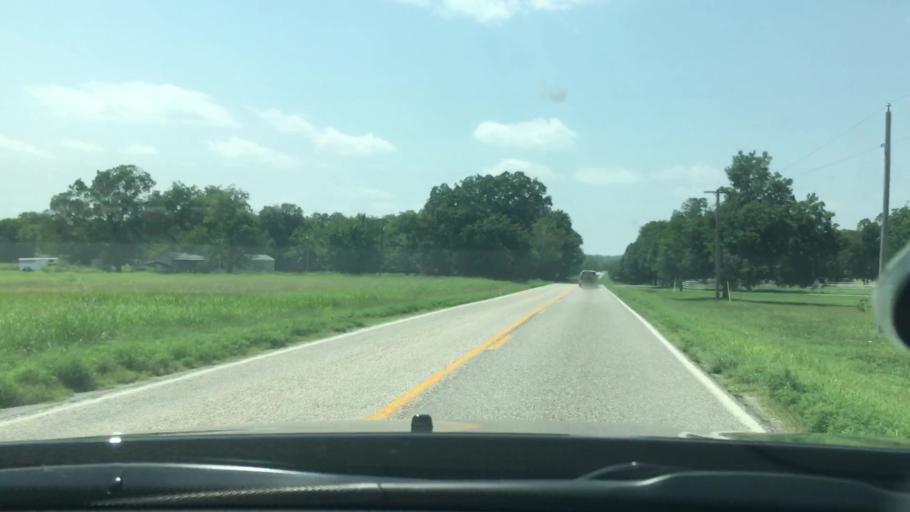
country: US
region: Oklahoma
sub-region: Coal County
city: Coalgate
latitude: 34.3750
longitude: -96.4340
